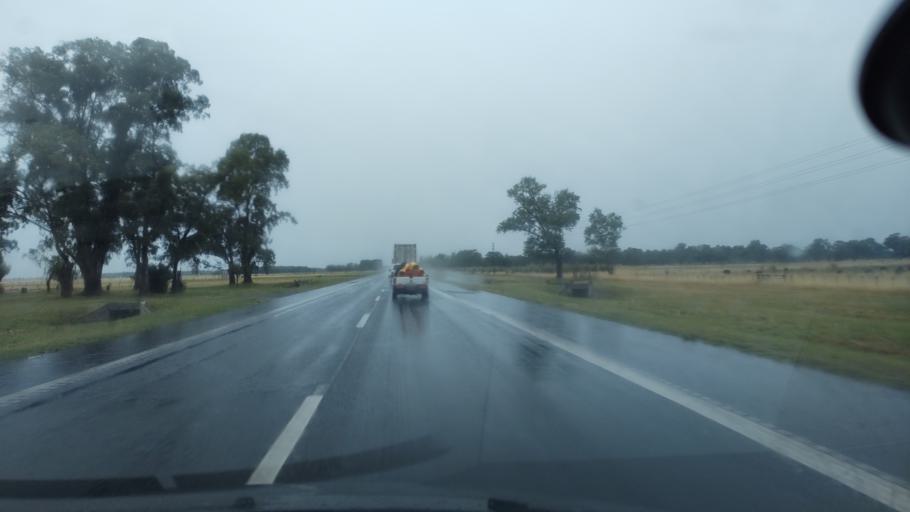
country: AR
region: Buenos Aires
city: Canuelas
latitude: -35.0653
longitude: -58.8246
